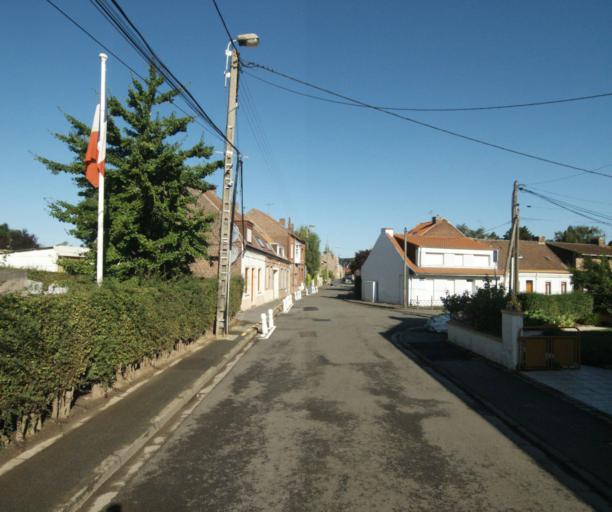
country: FR
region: Nord-Pas-de-Calais
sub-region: Departement du Nord
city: Toufflers
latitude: 50.6588
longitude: 3.2327
